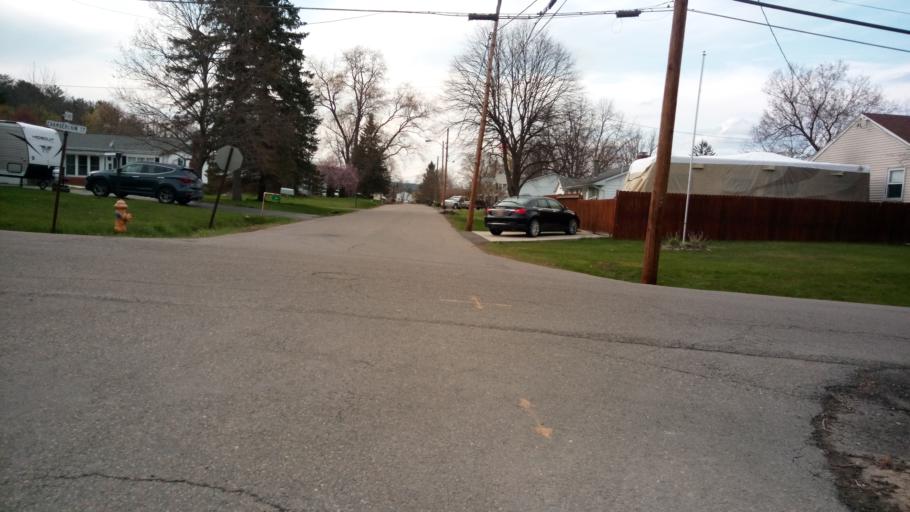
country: US
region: New York
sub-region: Chemung County
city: Southport
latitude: 42.0669
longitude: -76.8193
